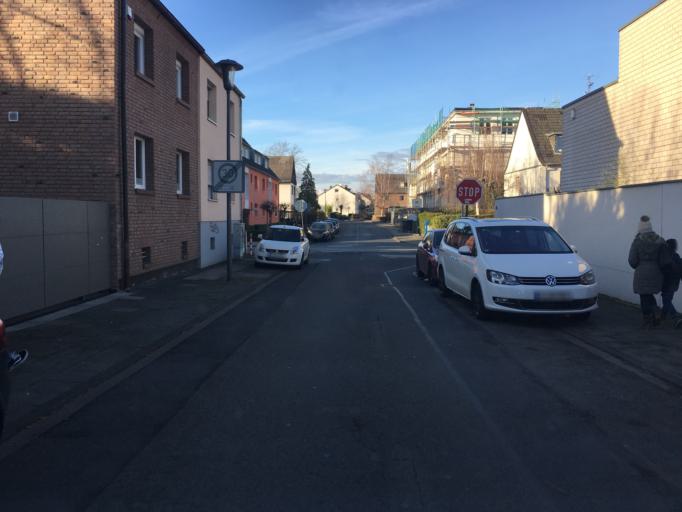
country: DE
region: North Rhine-Westphalia
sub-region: Regierungsbezirk Koln
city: Porz am Rhein
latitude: 50.8716
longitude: 7.0231
